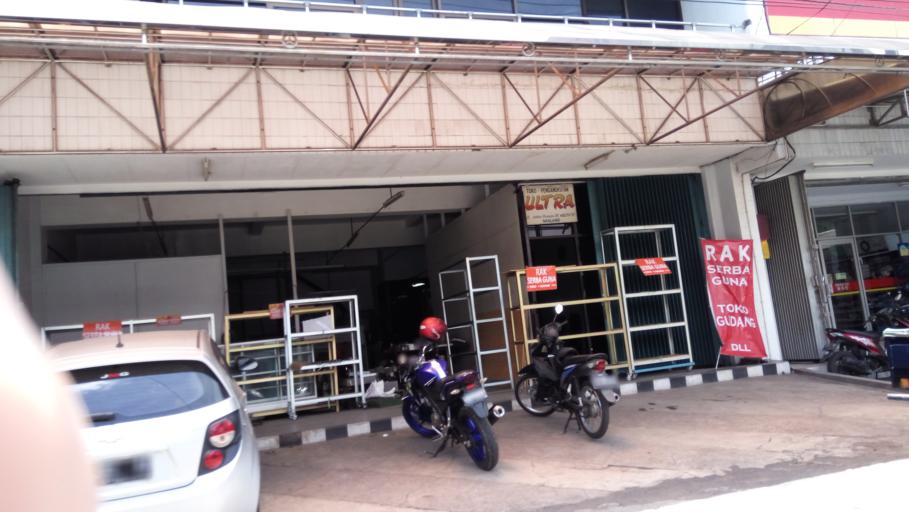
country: ID
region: East Java
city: Malang
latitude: -7.9859
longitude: 112.6260
